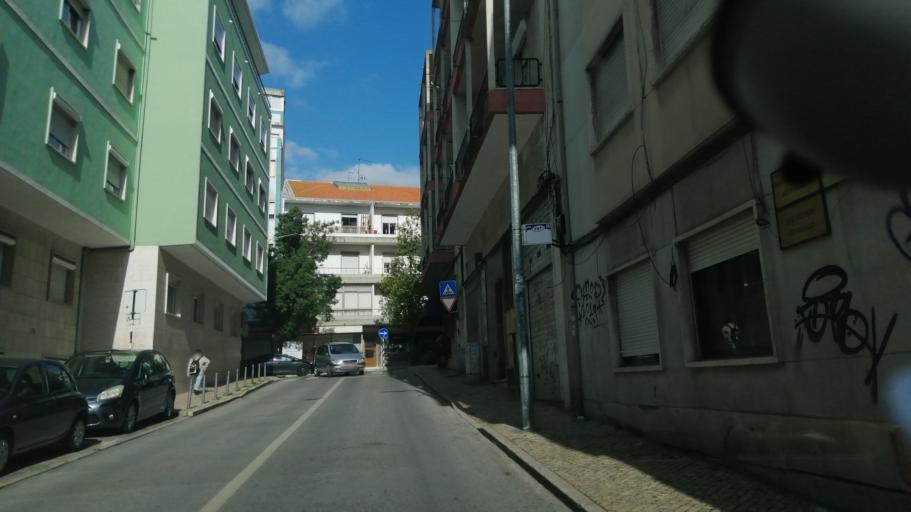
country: PT
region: Setubal
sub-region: Almada
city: Almada
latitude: 38.6795
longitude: -9.1601
